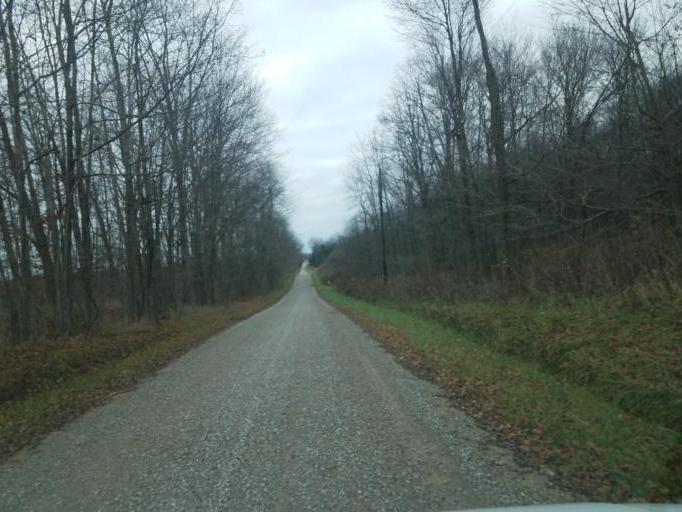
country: US
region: Ohio
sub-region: Knox County
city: Fredericktown
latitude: 40.5119
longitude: -82.6641
